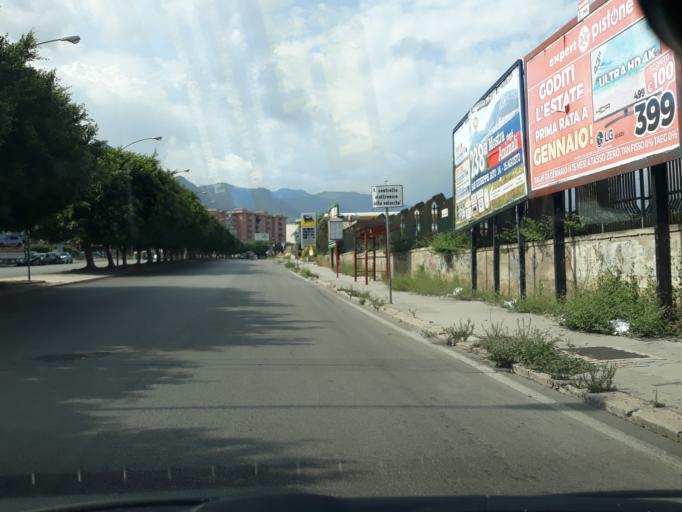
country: IT
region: Sicily
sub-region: Palermo
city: Palermo
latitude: 38.1007
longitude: 13.3473
